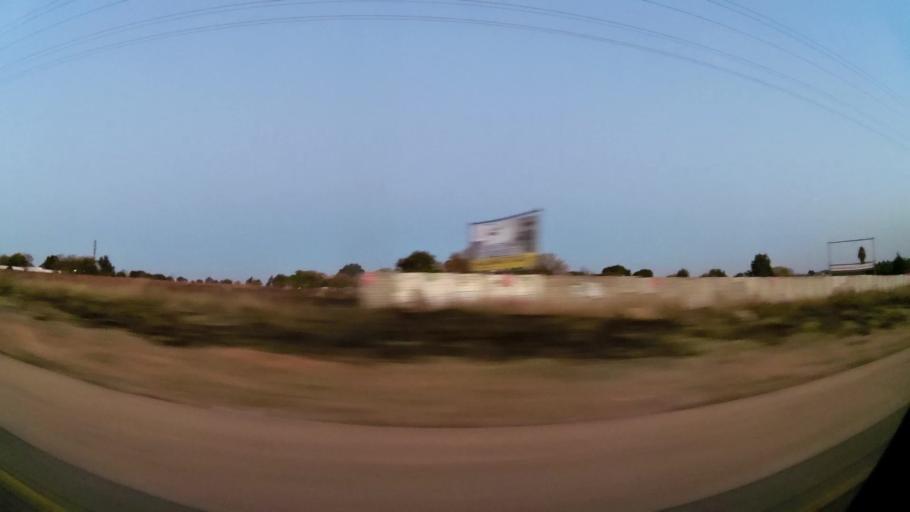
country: ZA
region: Gauteng
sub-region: City of Johannesburg Metropolitan Municipality
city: Midrand
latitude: -25.9435
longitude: 28.0935
